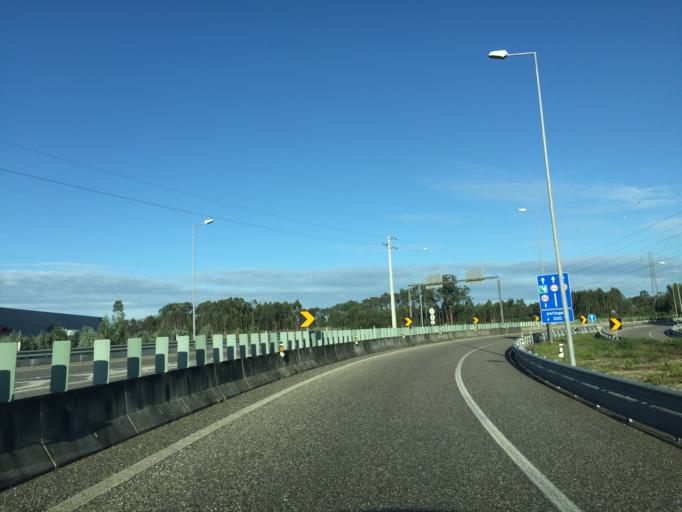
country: PT
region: Coimbra
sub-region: Figueira da Foz
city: Lavos
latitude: 40.0444
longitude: -8.8139
